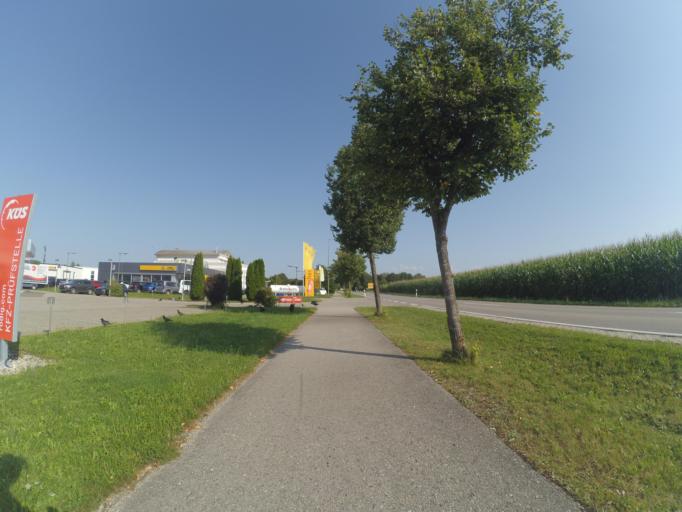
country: DE
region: Bavaria
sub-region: Swabia
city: Buchloe
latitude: 48.0426
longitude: 10.7044
